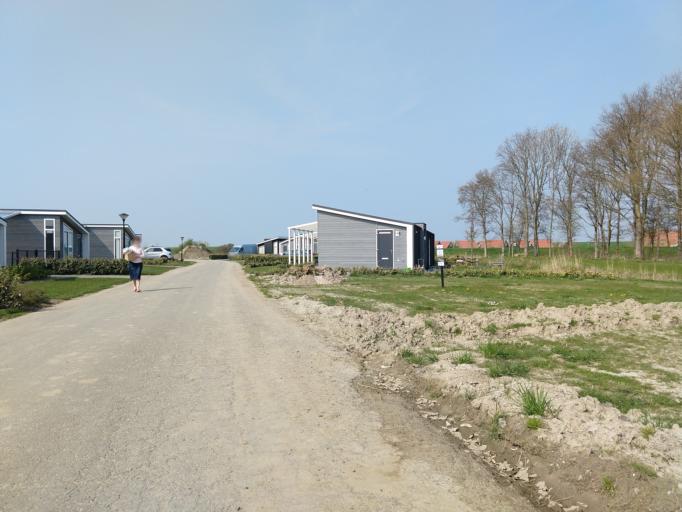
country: NL
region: Zeeland
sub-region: Gemeente Reimerswaal
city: Yerseke
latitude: 51.5225
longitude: 3.9808
